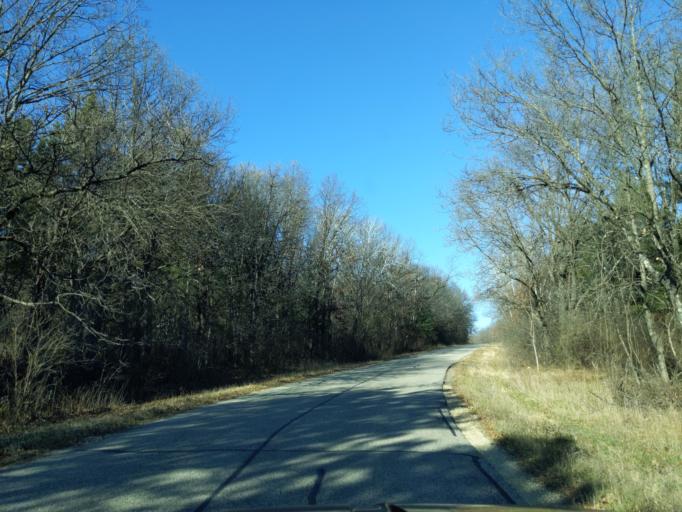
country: US
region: Wisconsin
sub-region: Waushara County
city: Wautoma
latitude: 44.1123
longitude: -89.2803
